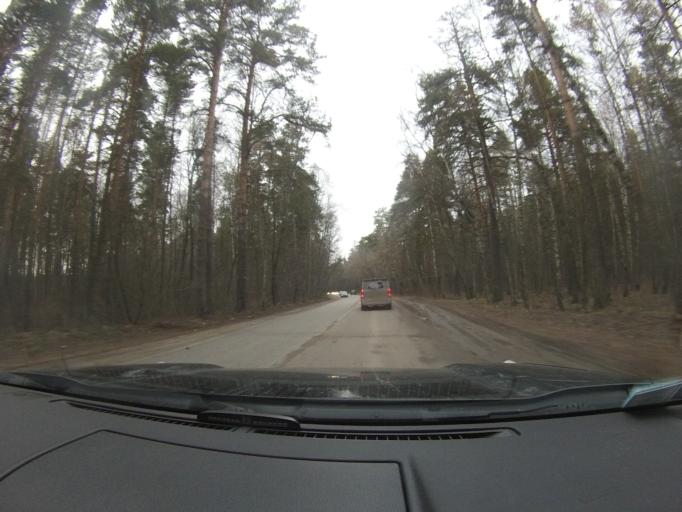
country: RU
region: Moskovskaya
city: Voskresensk
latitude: 55.3348
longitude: 38.6756
